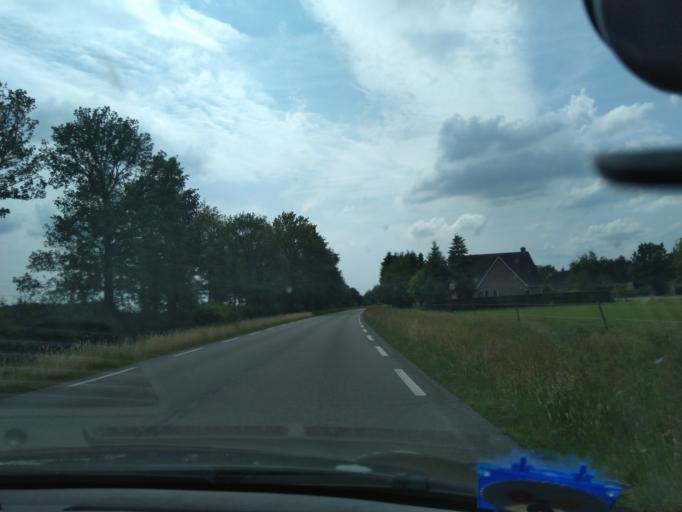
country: NL
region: Drenthe
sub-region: Gemeente Assen
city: Assen
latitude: 52.8988
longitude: 6.5366
